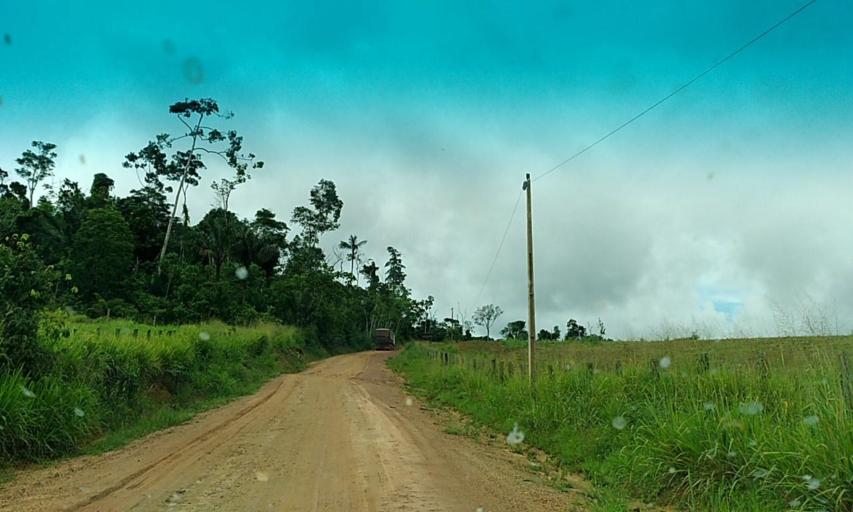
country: BR
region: Para
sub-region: Altamira
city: Altamira
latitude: -3.0715
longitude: -51.7094
